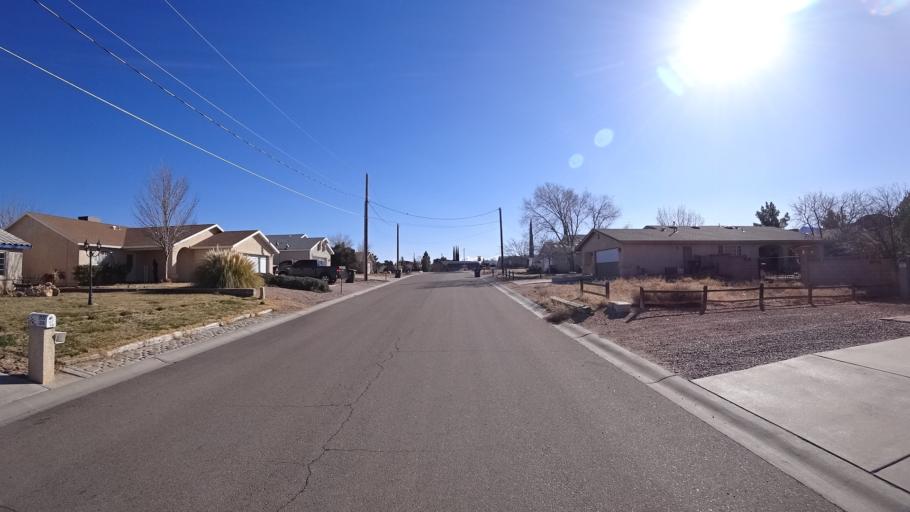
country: US
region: Arizona
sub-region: Mohave County
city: Kingman
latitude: 35.2041
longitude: -114.0123
